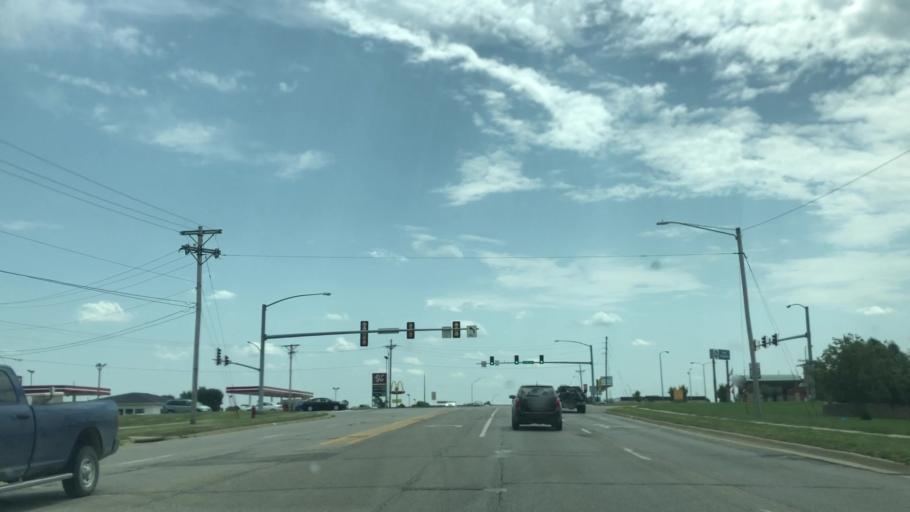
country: US
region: Iowa
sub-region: Marshall County
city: Marshalltown
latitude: 42.0078
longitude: -92.9124
